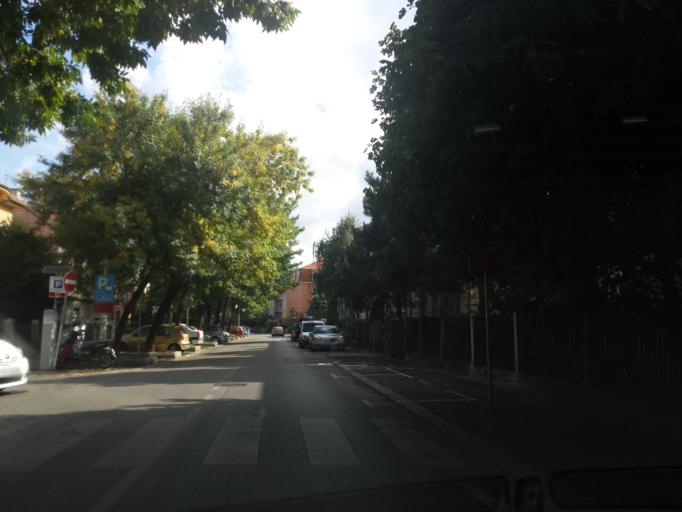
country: HR
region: Grad Zagreb
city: Zagreb
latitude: 45.8155
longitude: 16.0032
